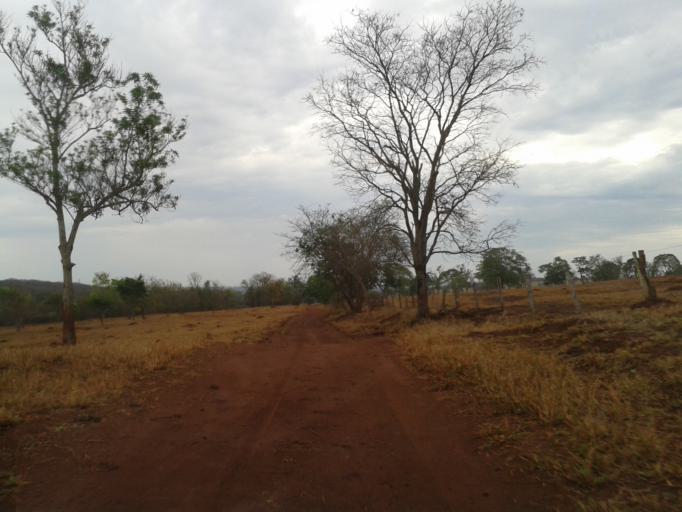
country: BR
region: Minas Gerais
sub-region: Santa Vitoria
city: Santa Vitoria
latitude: -18.8584
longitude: -49.8272
